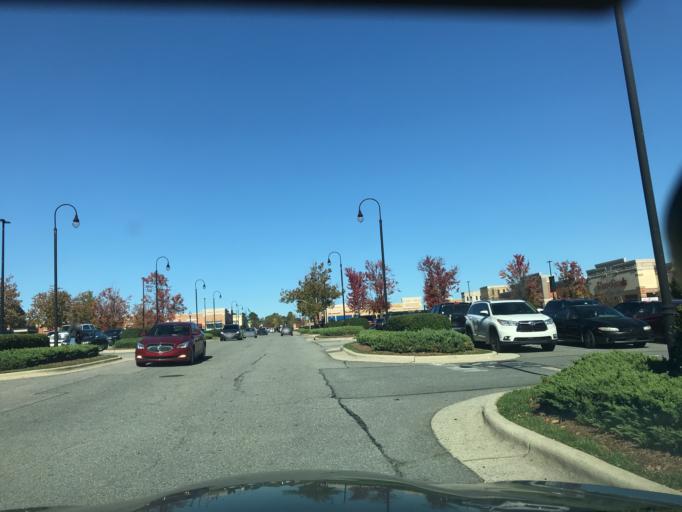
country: US
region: North Carolina
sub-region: Wake County
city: Morrisville
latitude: 35.9065
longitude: -78.7844
